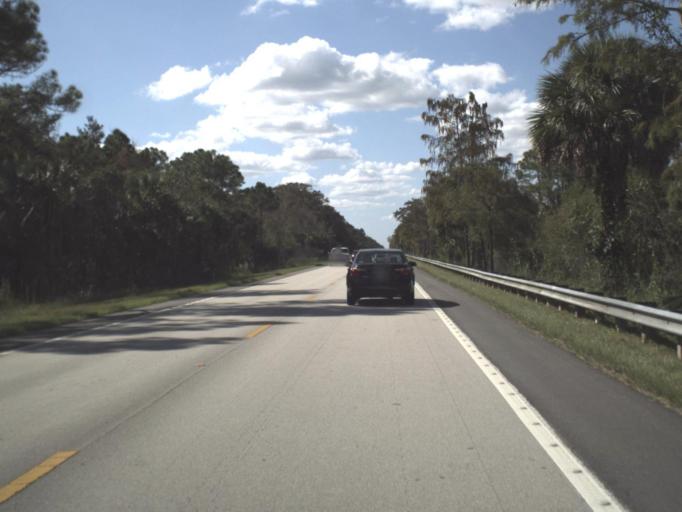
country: US
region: Florida
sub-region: Collier County
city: Marco
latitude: 25.8799
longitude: -81.2443
